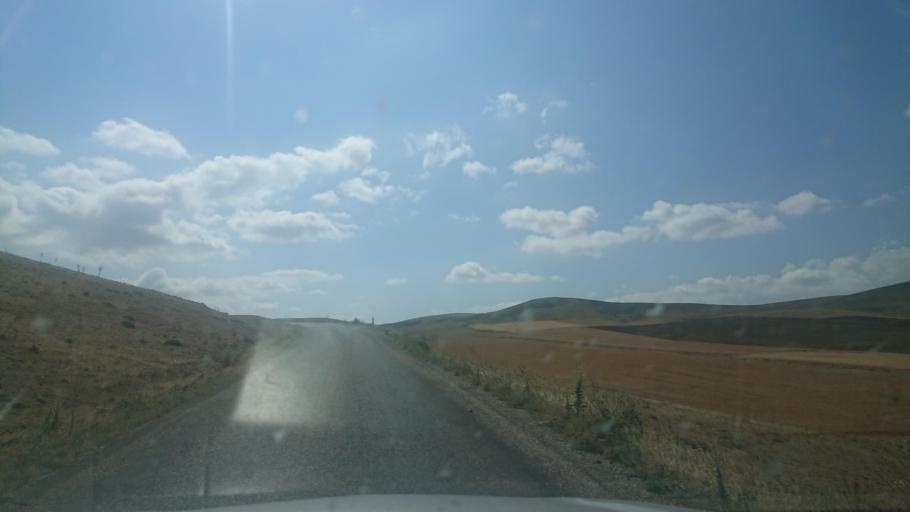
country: TR
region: Aksaray
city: Sariyahsi
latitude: 39.0070
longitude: 33.9521
